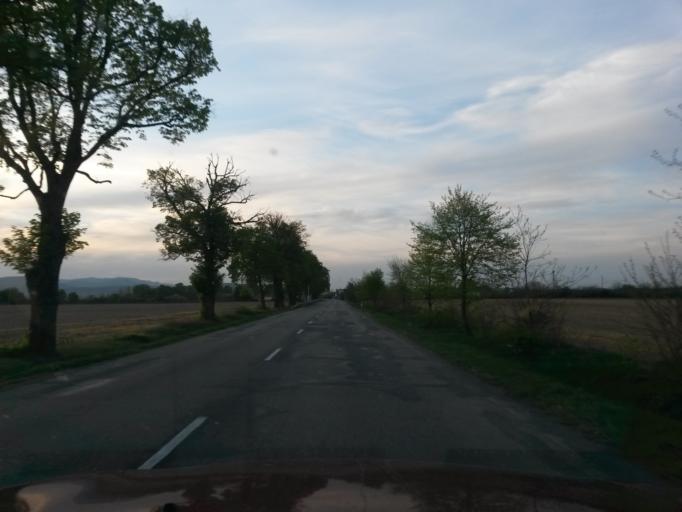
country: HU
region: Borsod-Abauj-Zemplen
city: Satoraljaujhely
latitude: 48.4553
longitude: 21.6467
